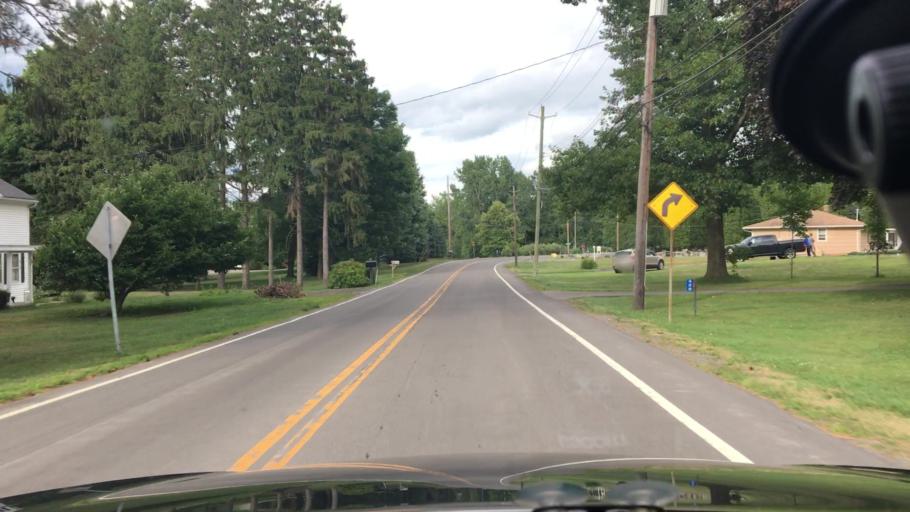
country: US
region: New York
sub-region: Erie County
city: Elma Center
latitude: 42.8219
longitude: -78.6602
